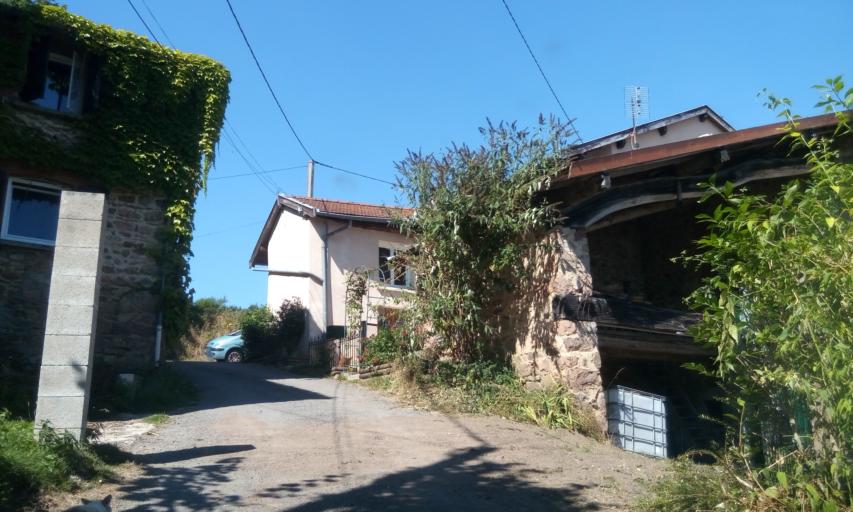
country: FR
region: Rhone-Alpes
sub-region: Departement du Rhone
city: Cublize
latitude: 45.9989
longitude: 4.4312
